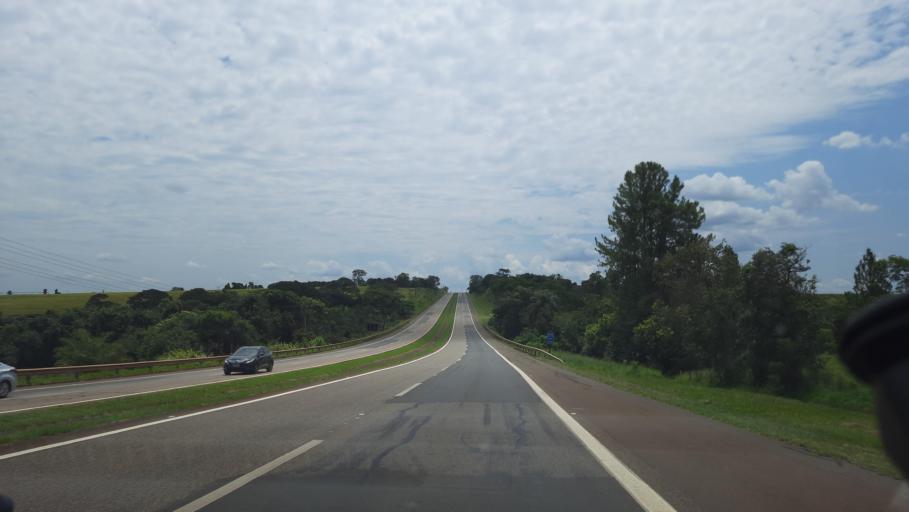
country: BR
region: Sao Paulo
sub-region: Casa Branca
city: Casa Branca
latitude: -21.7323
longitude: -47.0746
